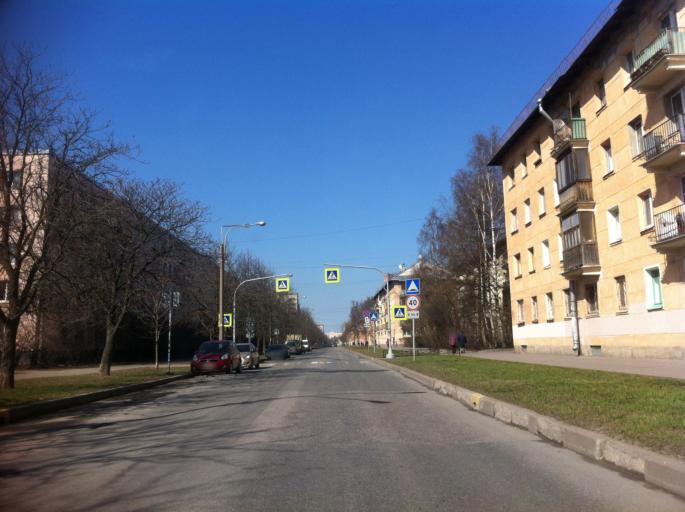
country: RU
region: St.-Petersburg
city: Dachnoye
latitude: 59.8349
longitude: 30.2564
